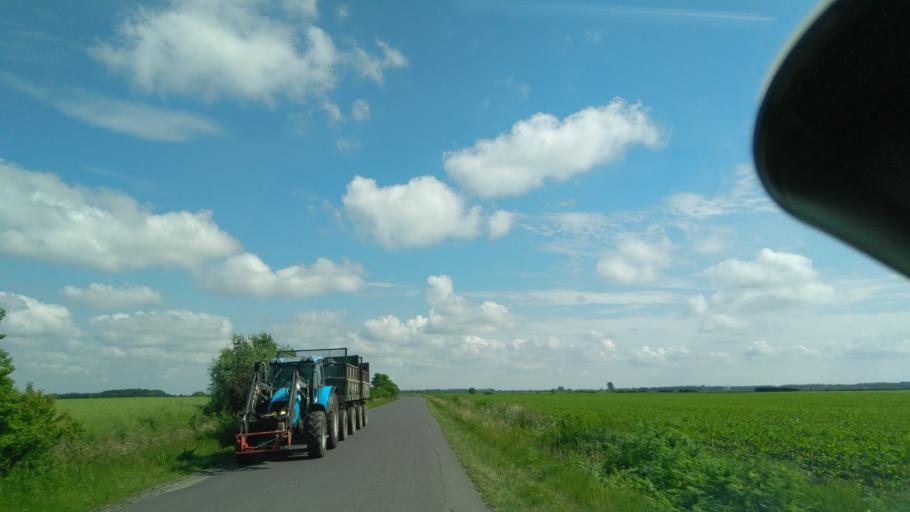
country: HU
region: Bekes
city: Bekes
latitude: 46.8143
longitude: 21.1481
